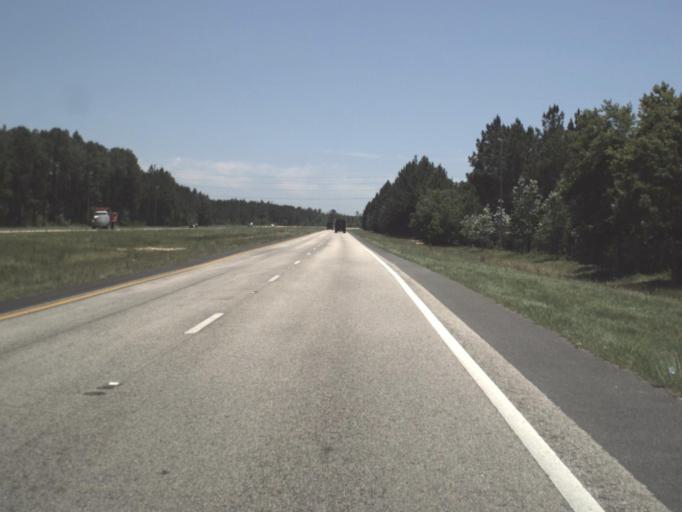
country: US
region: Florida
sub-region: Clay County
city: Bellair-Meadowbrook Terrace
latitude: 30.2258
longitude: -81.8421
